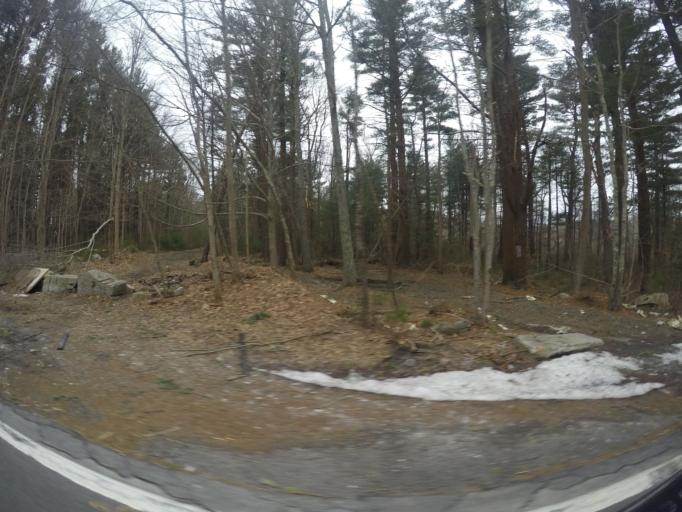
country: US
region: Massachusetts
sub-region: Bristol County
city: Easton
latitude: 42.0128
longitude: -71.0860
